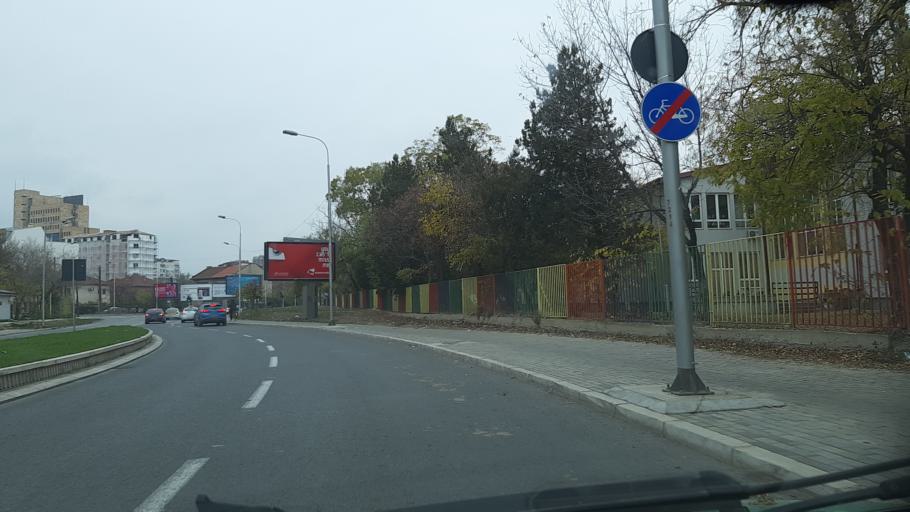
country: MK
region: Karpos
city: Skopje
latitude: 41.9886
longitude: 21.4405
